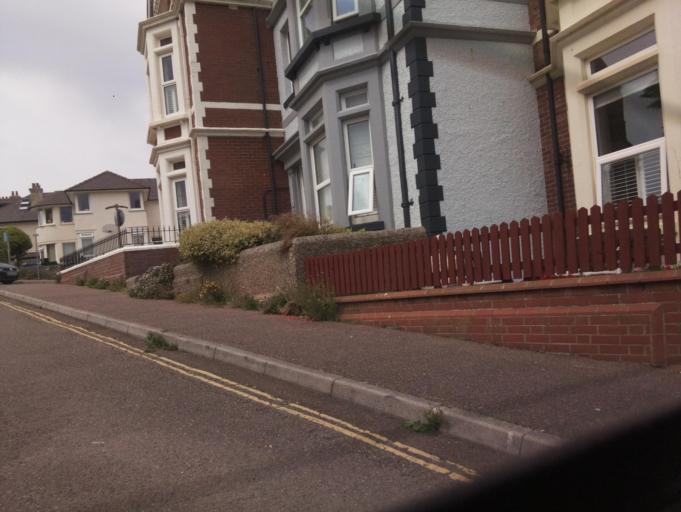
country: GB
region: England
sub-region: Devon
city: Colyton
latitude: 50.7041
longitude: -3.0718
